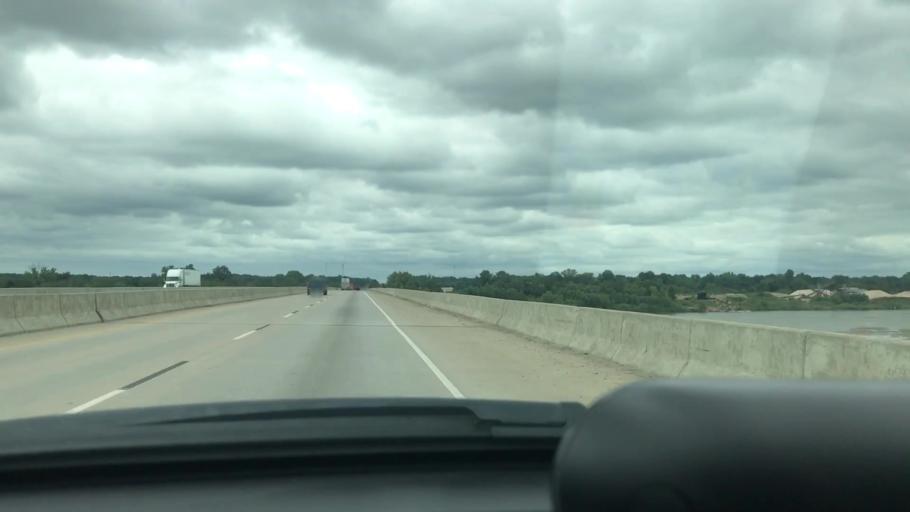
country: US
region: Oklahoma
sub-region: Muskogee County
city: Muskogee
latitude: 35.8055
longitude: -95.4018
